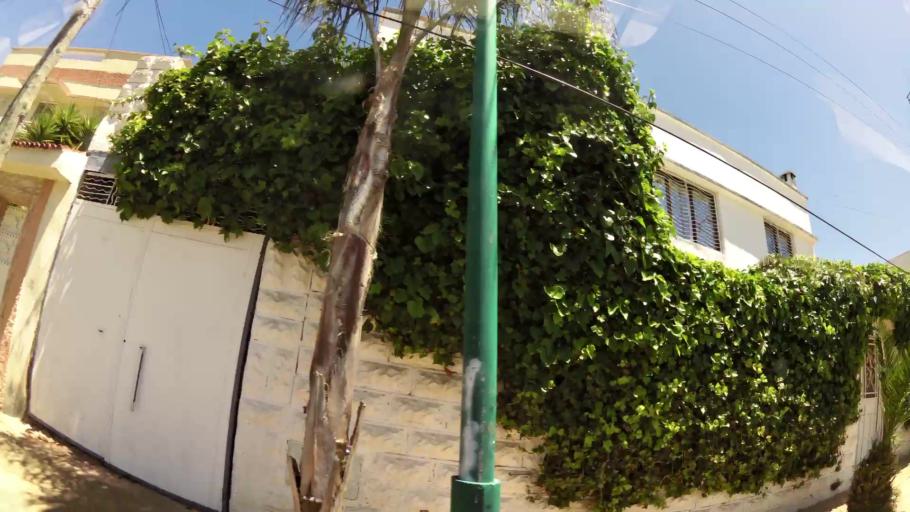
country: MA
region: Meknes-Tafilalet
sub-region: Meknes
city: Meknes
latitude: 33.9075
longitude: -5.5620
